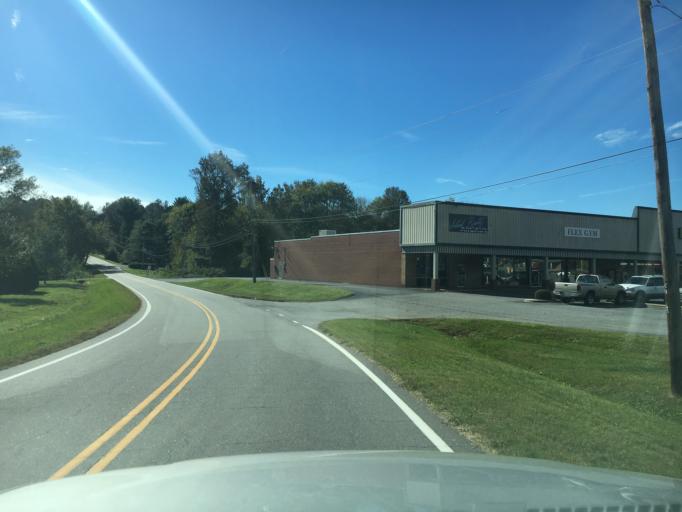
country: US
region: North Carolina
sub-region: Burke County
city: Morganton
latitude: 35.7342
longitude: -81.7100
